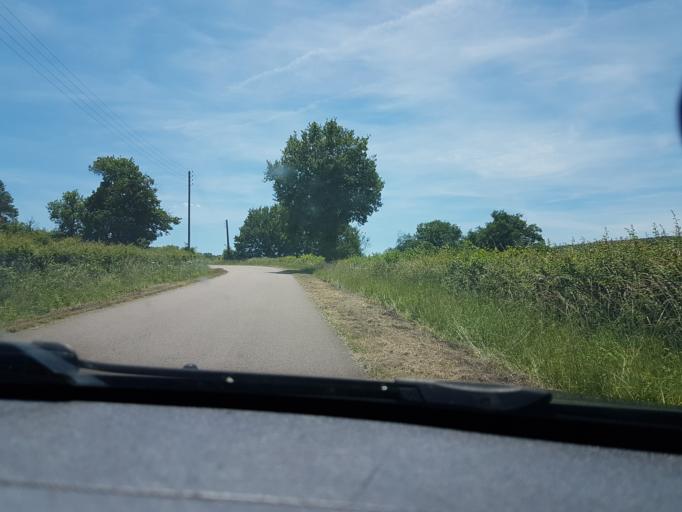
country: FR
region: Bourgogne
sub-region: Departement de Saone-et-Loire
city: Epinac
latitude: 46.9765
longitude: 4.5046
